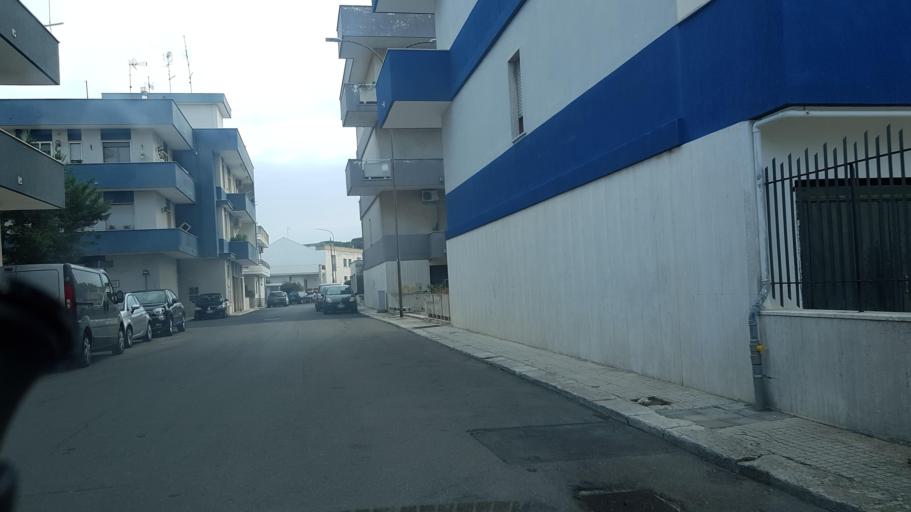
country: IT
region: Apulia
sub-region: Provincia di Lecce
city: Trepuzzi
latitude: 40.4032
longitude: 18.0705
